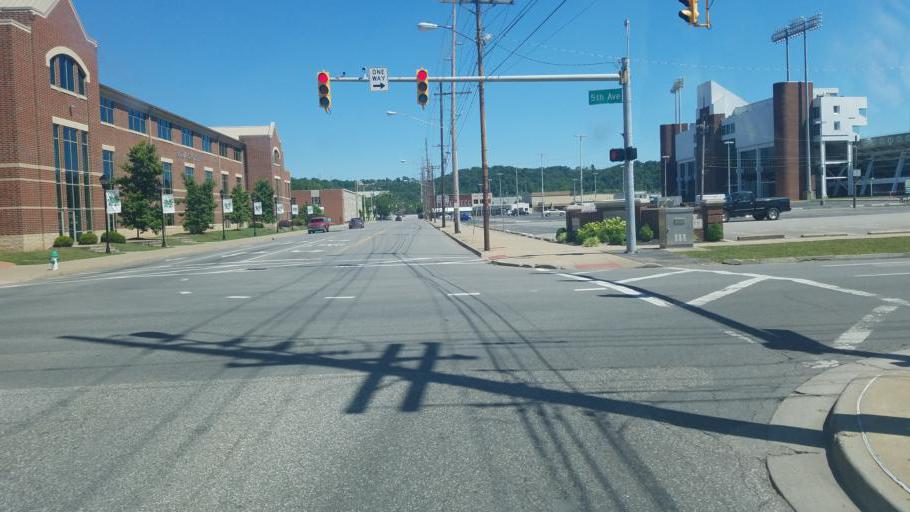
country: US
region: West Virginia
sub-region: Cabell County
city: Huntington
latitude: 38.4229
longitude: -82.4225
